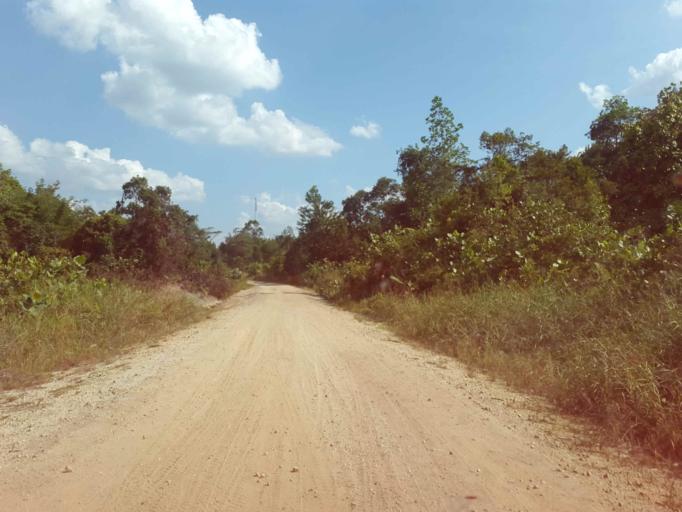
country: MY
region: Sarawak
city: Simanggang
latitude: 0.7116
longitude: 111.5370
